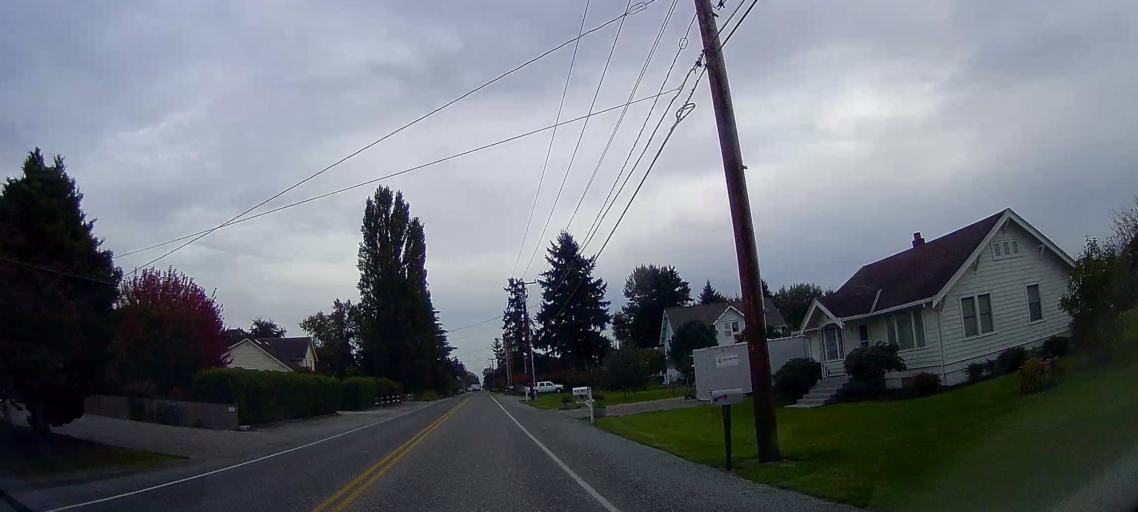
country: US
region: Washington
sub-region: Skagit County
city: Mount Vernon
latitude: 48.4454
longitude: -122.3787
